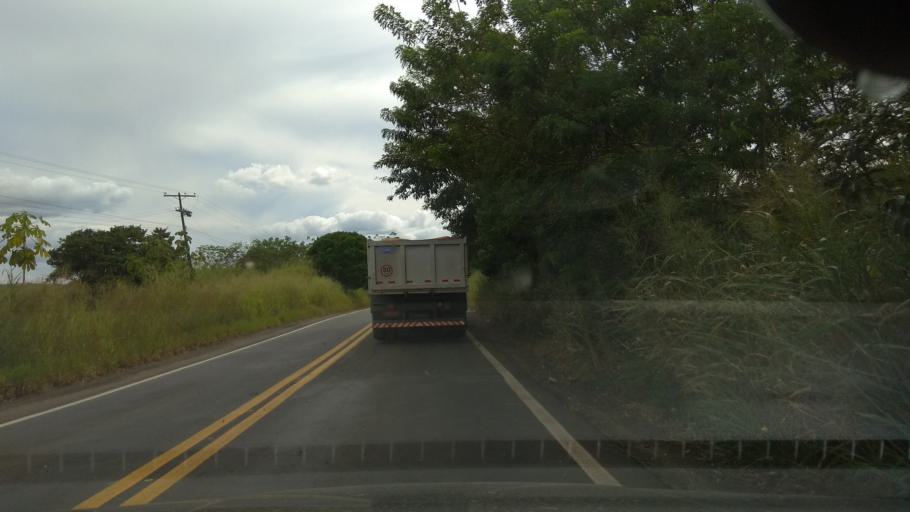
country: BR
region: Bahia
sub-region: Ubata
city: Ubata
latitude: -14.1971
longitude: -39.6186
